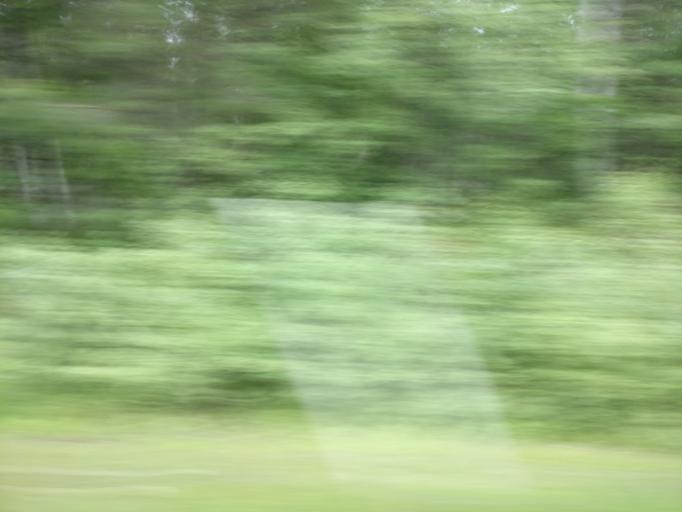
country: FI
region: Southern Savonia
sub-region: Savonlinna
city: Rantasalmi
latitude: 62.1509
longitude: 28.1703
